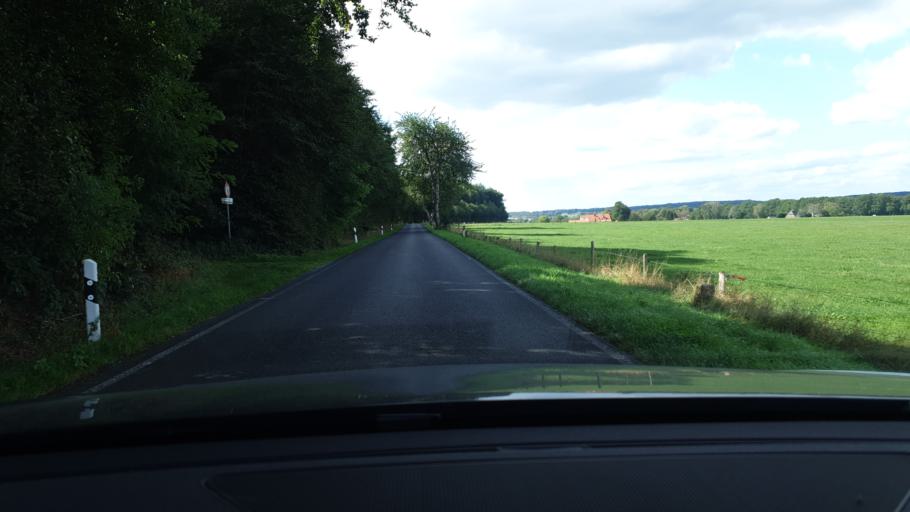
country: NL
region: Gelderland
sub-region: Gemeente Groesbeek
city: De Horst
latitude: 51.7616
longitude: 5.9817
